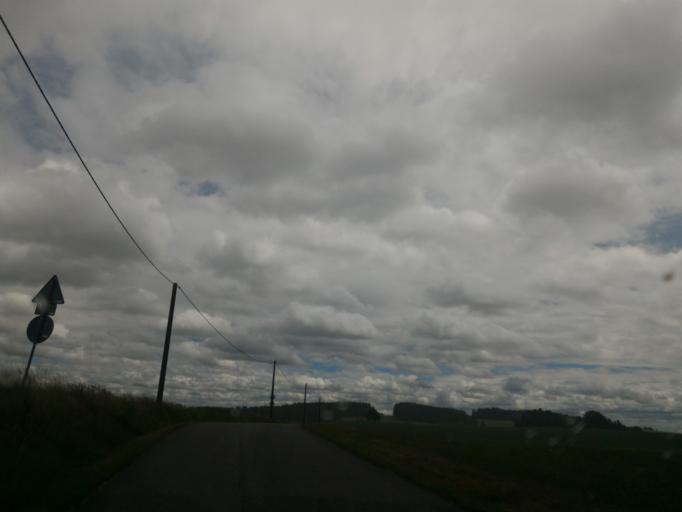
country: CZ
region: Vysocina
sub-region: Okres Jihlava
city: Telc
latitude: 49.2448
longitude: 15.4264
